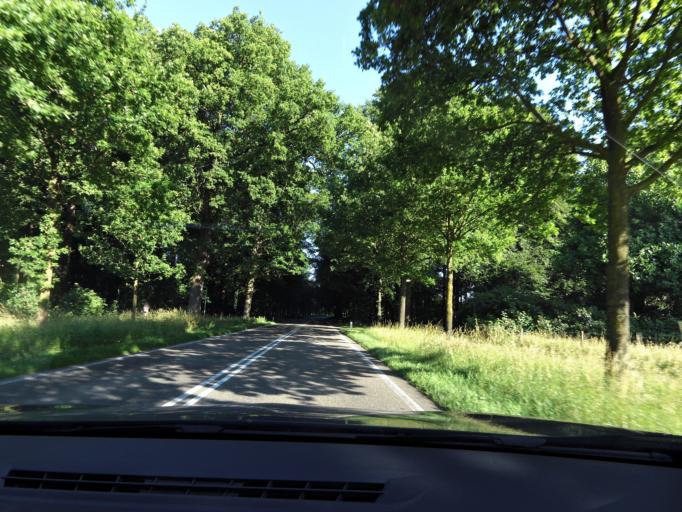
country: NL
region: Gelderland
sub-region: Gemeente Voorst
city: Twello
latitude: 52.2192
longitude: 6.1140
